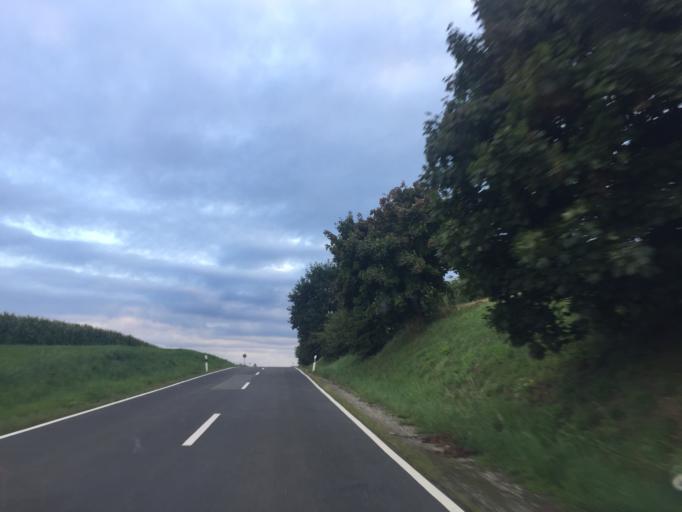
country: DE
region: Bavaria
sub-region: Upper Palatinate
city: Kirchendemenreuth
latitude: 49.7812
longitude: 12.0976
